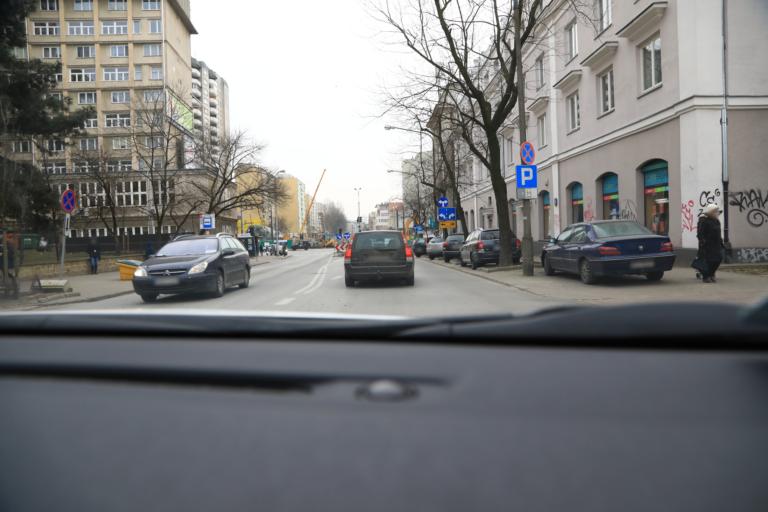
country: PL
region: Masovian Voivodeship
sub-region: Warszawa
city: Wola
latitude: 52.2344
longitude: 20.9657
